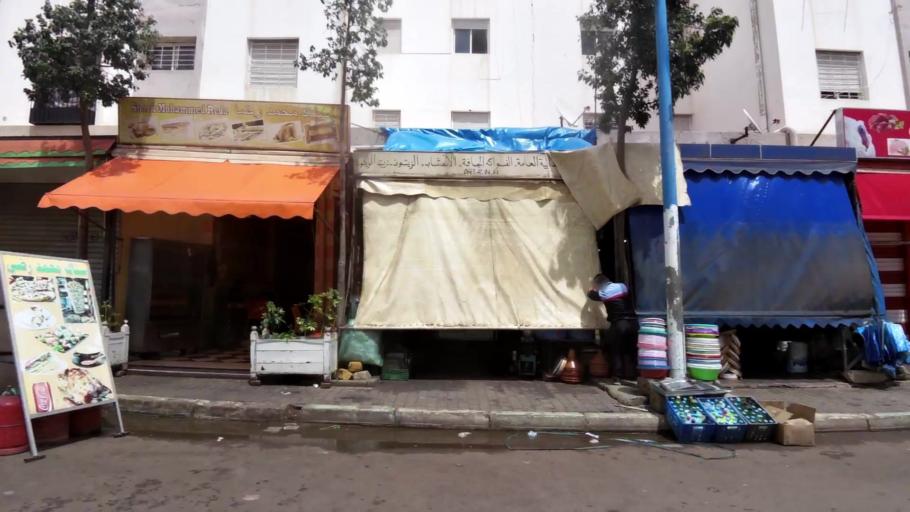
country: MA
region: Grand Casablanca
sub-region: Casablanca
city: Casablanca
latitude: 33.5411
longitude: -7.6964
